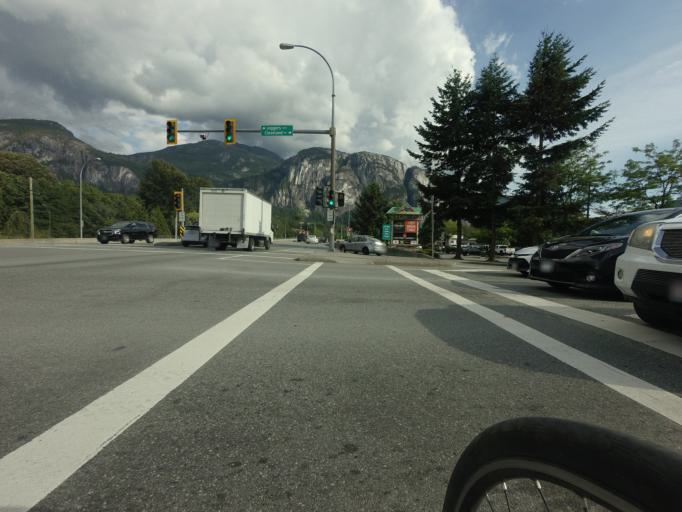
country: CA
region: British Columbia
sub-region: Greater Vancouver Regional District
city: Lions Bay
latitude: 49.7043
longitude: -123.1458
